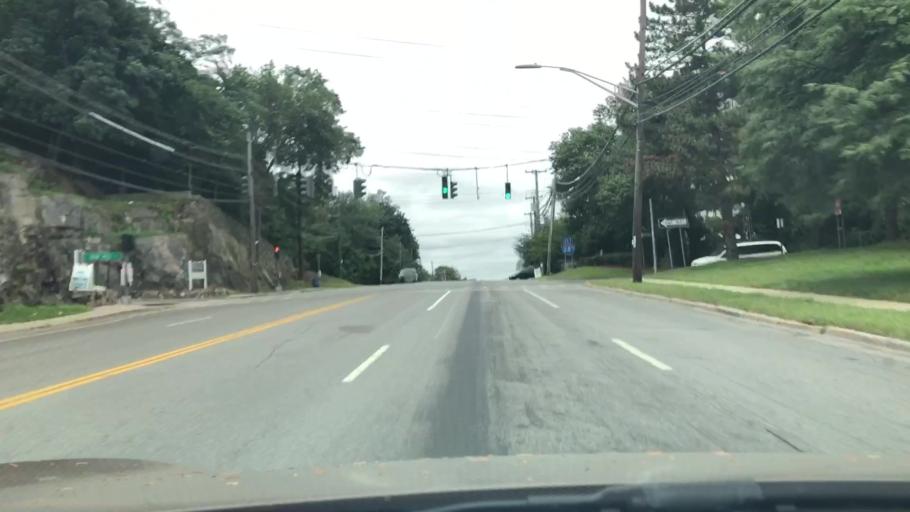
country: US
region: New York
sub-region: Westchester County
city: Elmsford
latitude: 41.0564
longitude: -73.8229
